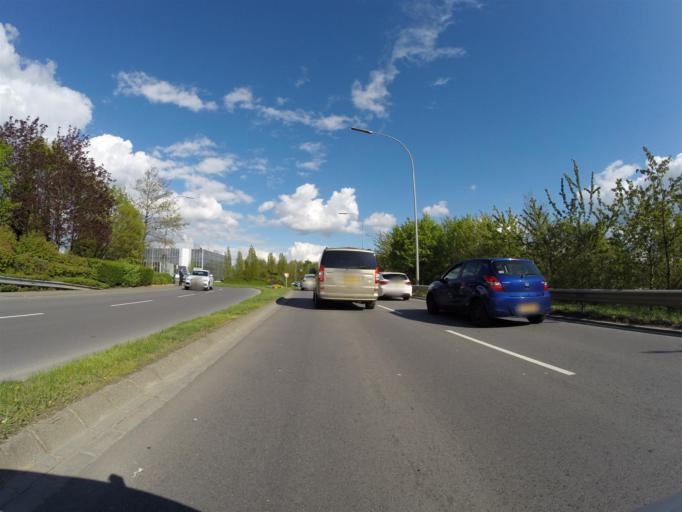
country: LU
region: Luxembourg
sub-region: Canton de Luxembourg
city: Hesperange
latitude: 49.5782
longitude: 6.1324
